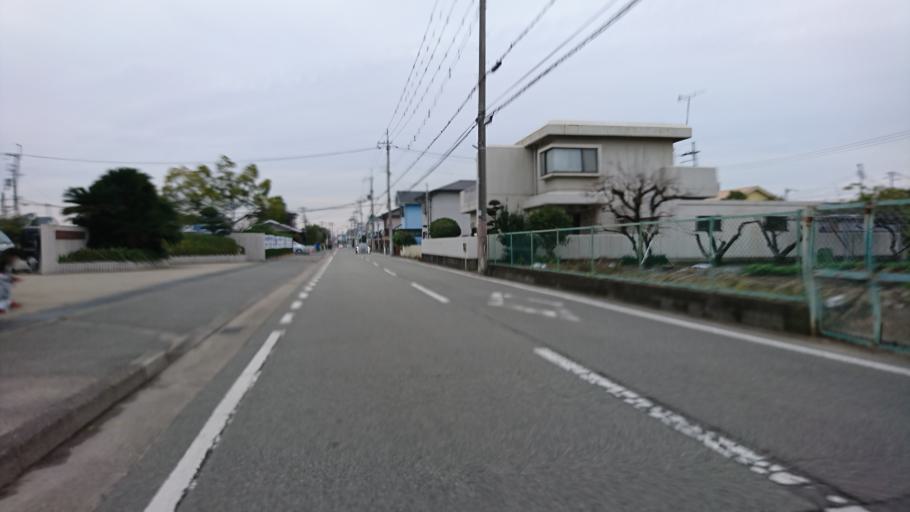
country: JP
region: Hyogo
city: Kakogawacho-honmachi
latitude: 34.7675
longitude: 134.8182
